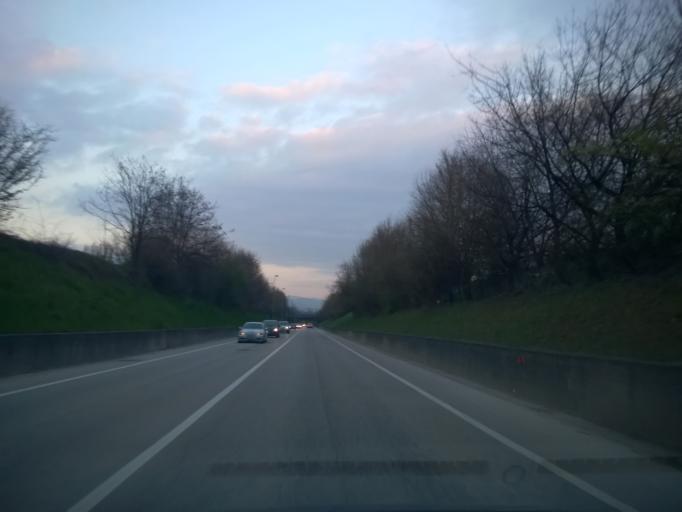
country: IT
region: Veneto
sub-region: Provincia di Vicenza
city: Schio
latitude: 45.7088
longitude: 11.3787
